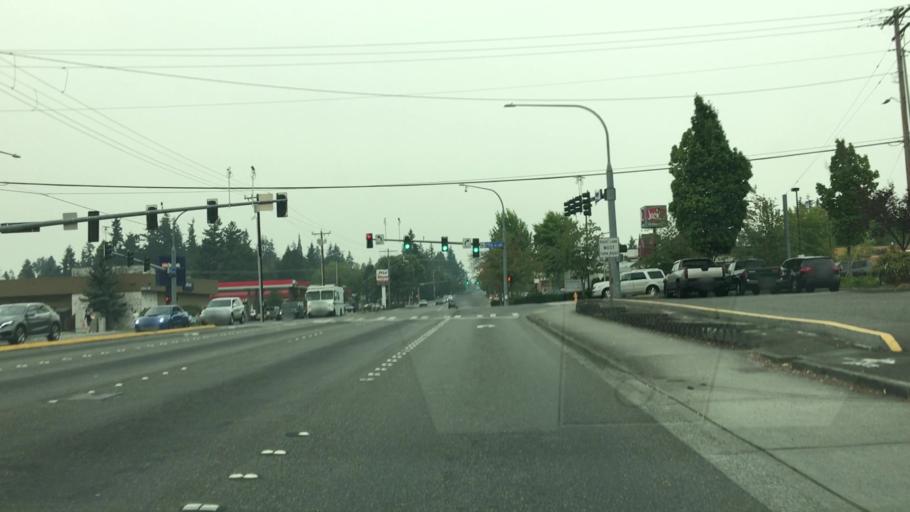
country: US
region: Washington
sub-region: Snohomish County
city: Alderwood Manor
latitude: 47.8204
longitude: -122.2922
